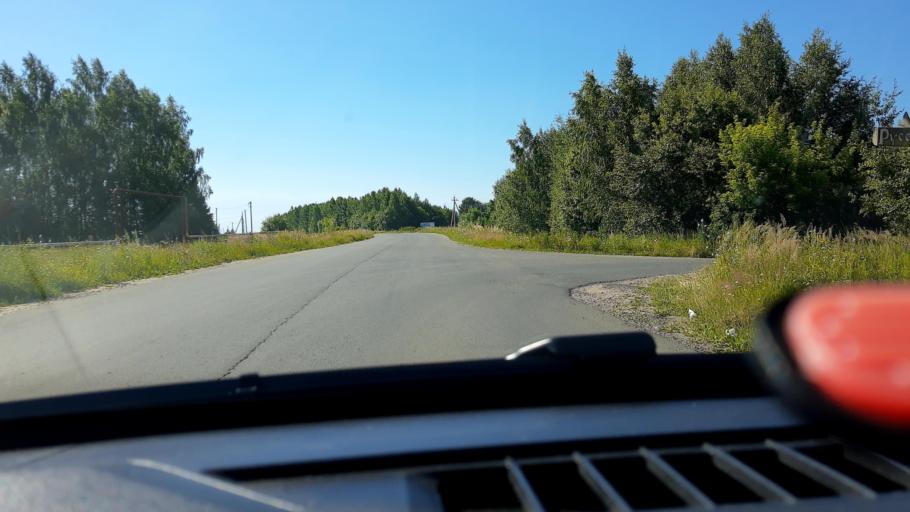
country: RU
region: Nizjnij Novgorod
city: Babino
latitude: 56.1353
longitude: 43.6428
